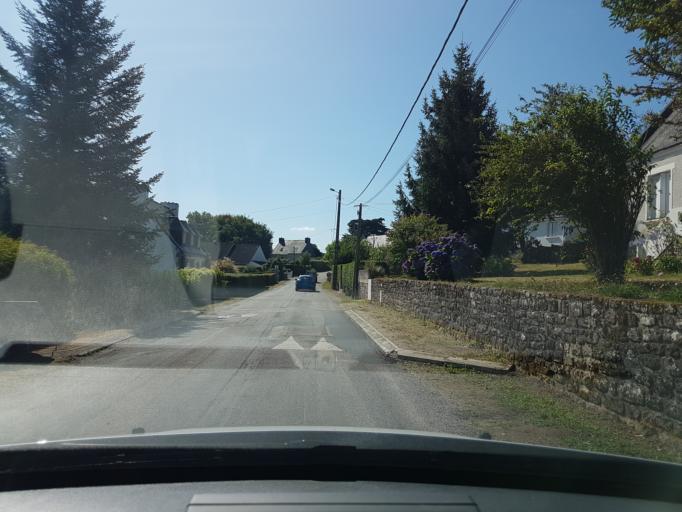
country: FR
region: Brittany
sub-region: Departement du Morbihan
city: Belz
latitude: 47.6783
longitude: -3.1818
